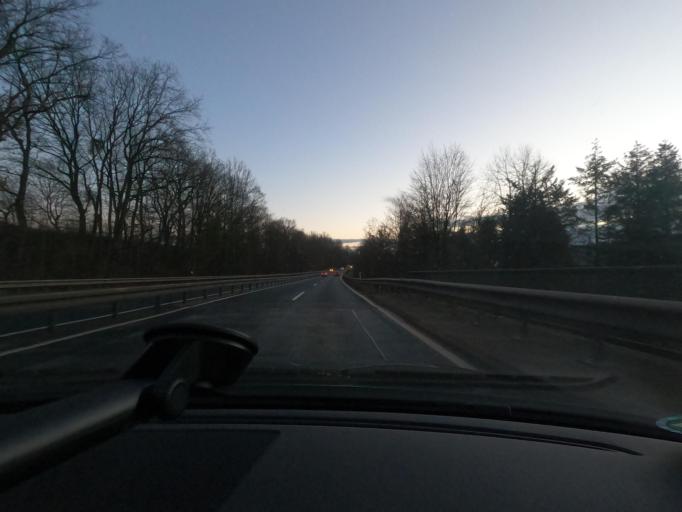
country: DE
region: Lower Saxony
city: Badenhausen
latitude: 51.7682
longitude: 10.2169
